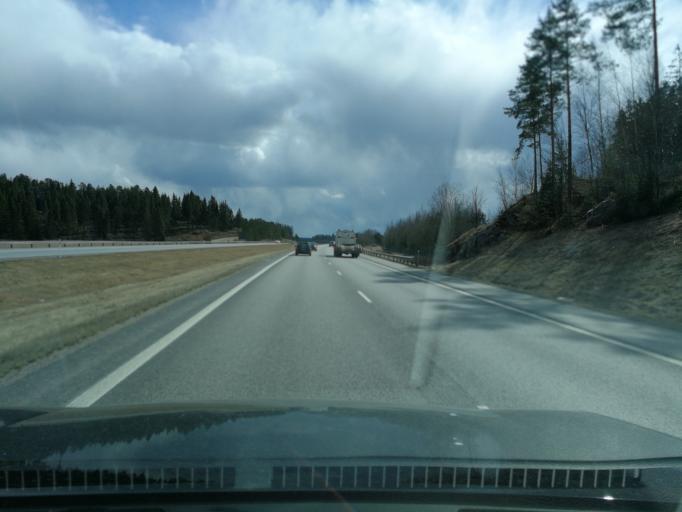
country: FI
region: Varsinais-Suomi
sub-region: Turku
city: Paimio
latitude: 60.4404
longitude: 22.6215
